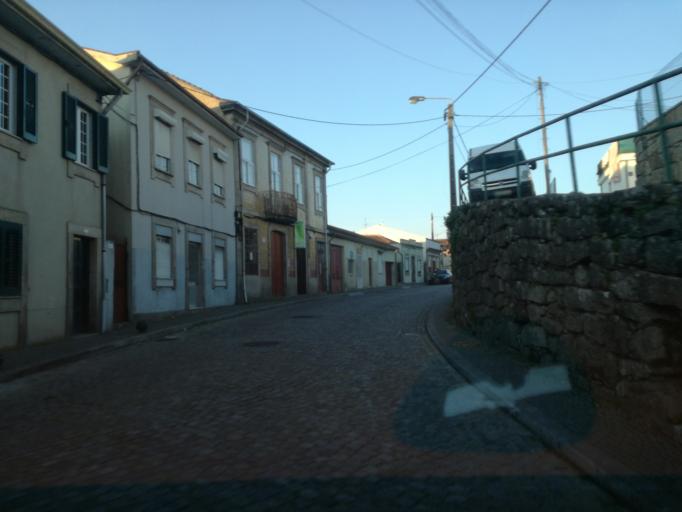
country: PT
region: Porto
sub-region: Maia
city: Milheiros
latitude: 41.2183
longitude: -8.5920
